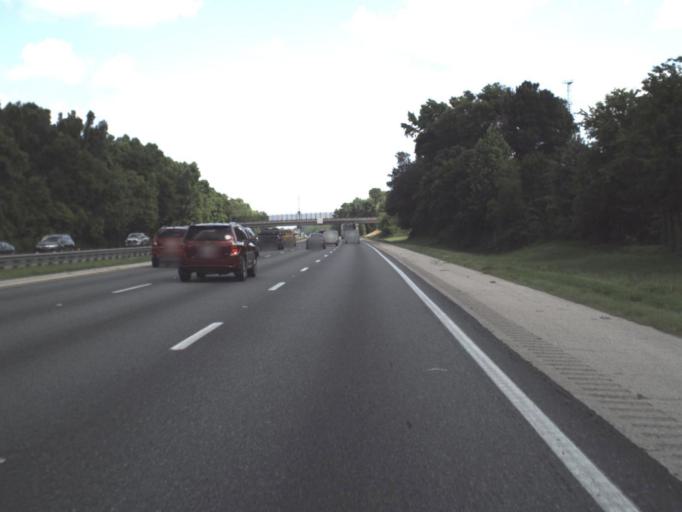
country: US
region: Florida
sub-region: Alachua County
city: Gainesville
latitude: 29.6372
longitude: -82.3999
